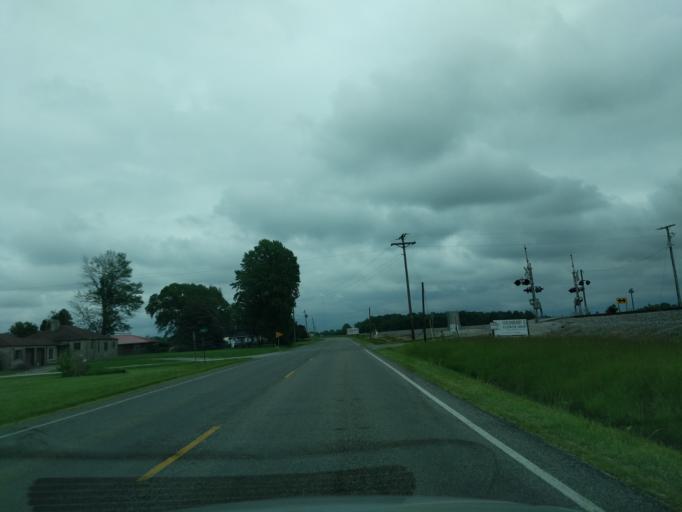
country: US
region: Indiana
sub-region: Madison County
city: Elwood
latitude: 40.2771
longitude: -85.8804
